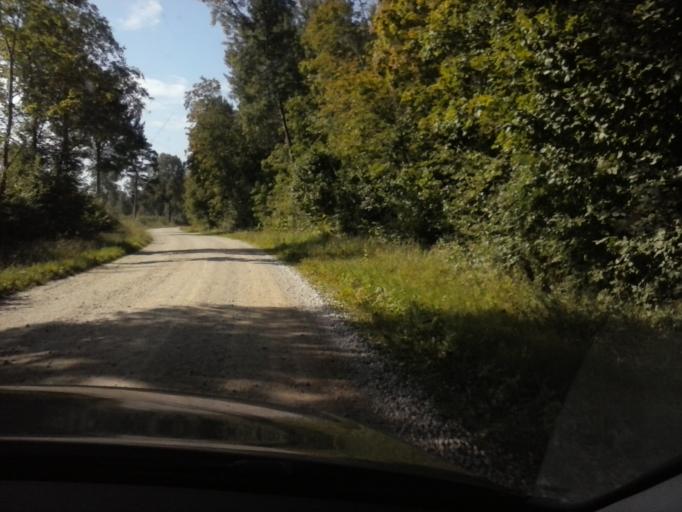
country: EE
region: Laeaene
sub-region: Haapsalu linn
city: Haapsalu
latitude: 58.8779
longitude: 23.5584
